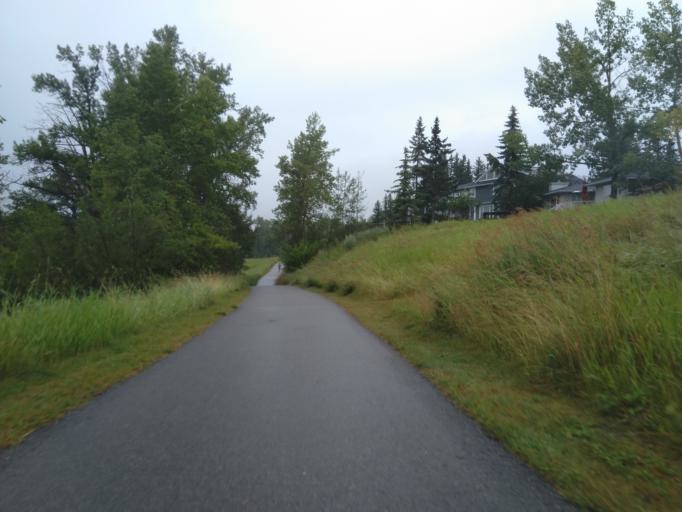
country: CA
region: Alberta
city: Cochrane
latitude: 51.1793
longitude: -114.4787
